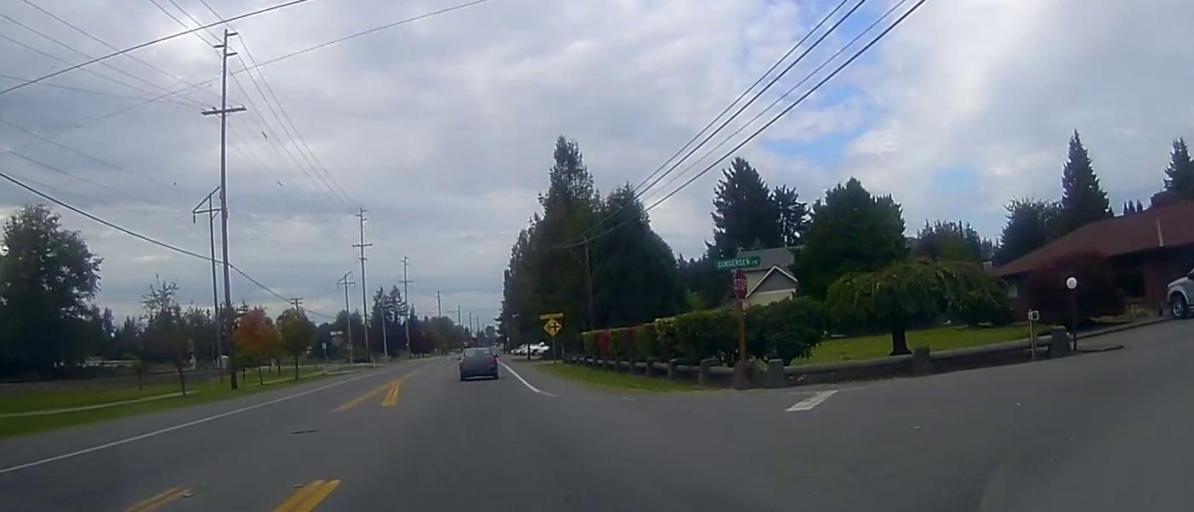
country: US
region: Washington
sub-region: Skagit County
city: Burlington
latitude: 48.4848
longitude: -122.3015
